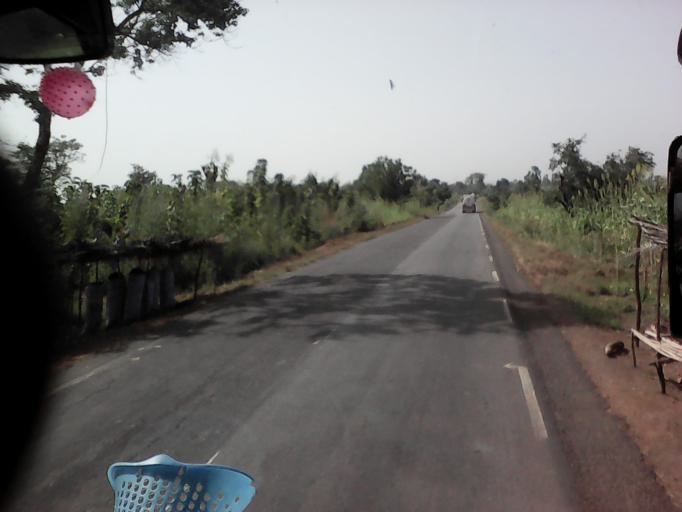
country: TG
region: Centrale
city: Sokode
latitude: 8.7875
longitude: 1.0678
